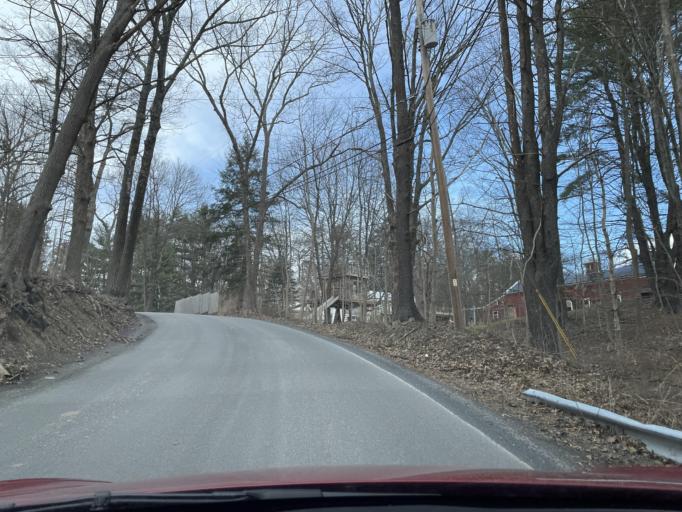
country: US
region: New York
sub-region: Ulster County
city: Saugerties
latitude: 42.1074
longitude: -73.9835
